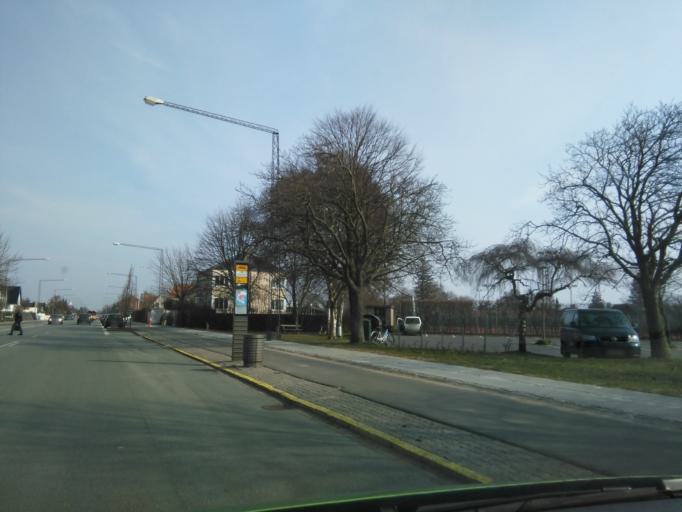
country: DK
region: Central Jutland
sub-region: Arhus Kommune
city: Lystrup
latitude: 56.1947
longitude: 10.2465
